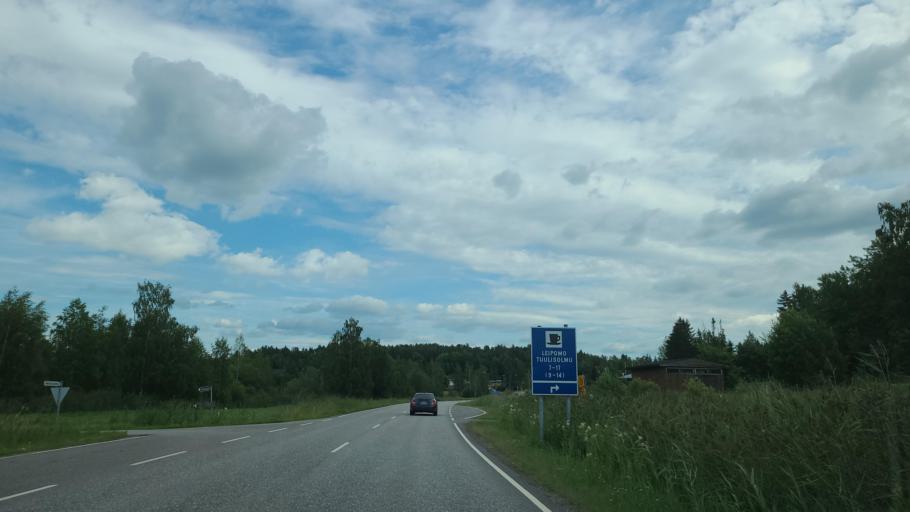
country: FI
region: Varsinais-Suomi
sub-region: Turku
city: Rymaettylae
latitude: 60.3799
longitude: 21.9426
